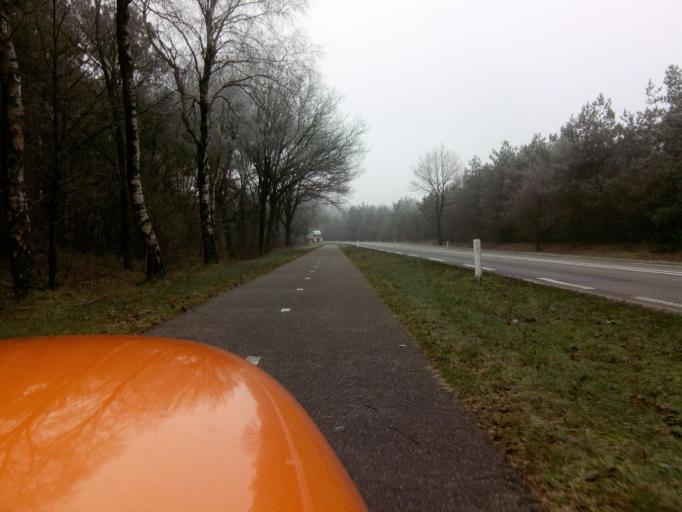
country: NL
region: Gelderland
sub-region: Gemeente Apeldoorn
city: Uddel
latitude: 52.2505
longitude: 5.7469
